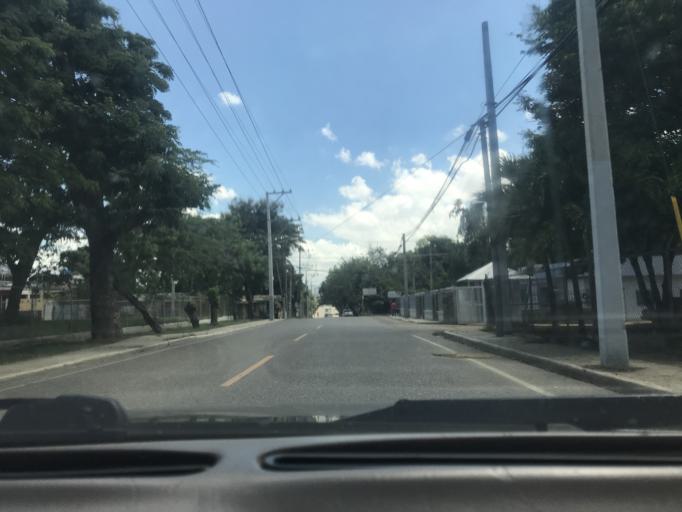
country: DO
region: Santiago
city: Santiago de los Caballeros
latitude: 19.4098
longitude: -70.7184
